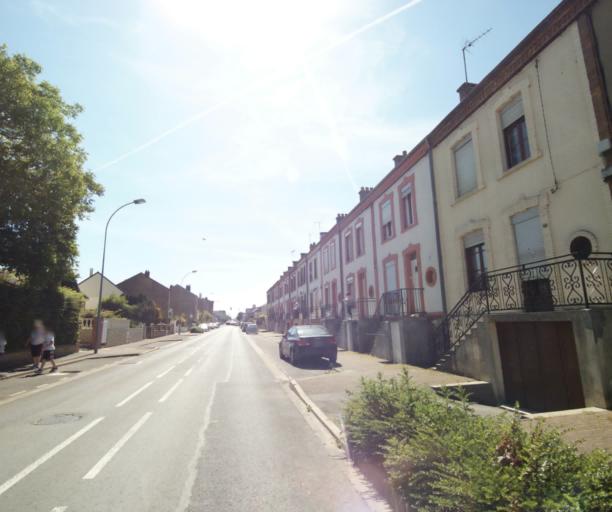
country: FR
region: Champagne-Ardenne
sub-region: Departement des Ardennes
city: Villers-Semeuse
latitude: 49.7438
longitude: 4.7379
